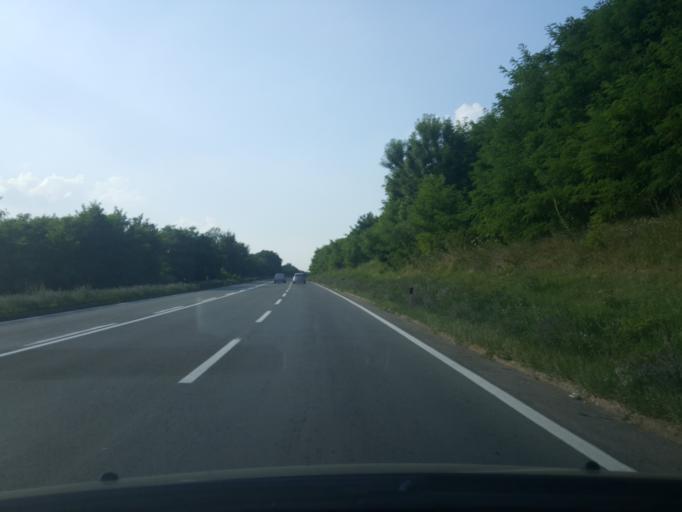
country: RS
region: Central Serbia
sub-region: Belgrade
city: Mladenovac
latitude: 44.5069
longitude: 20.6555
